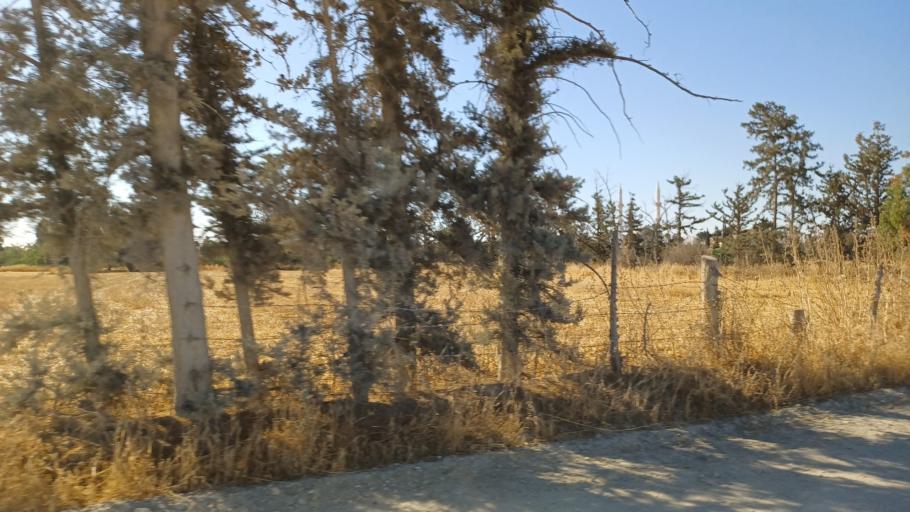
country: CY
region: Larnaka
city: Pergamos
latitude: 35.0421
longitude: 33.7032
